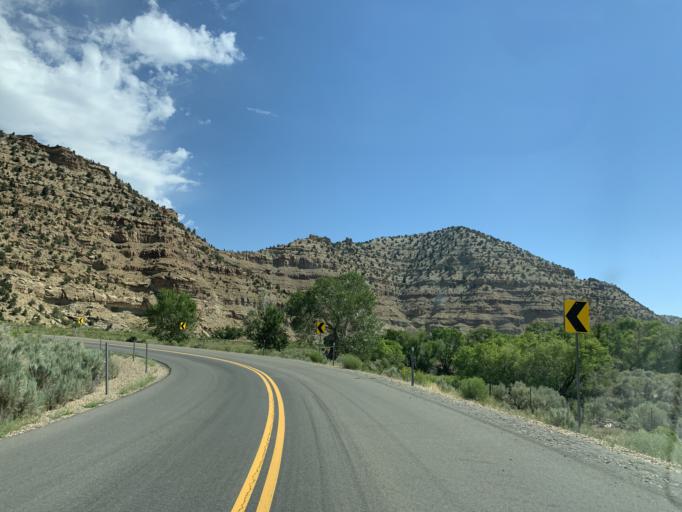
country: US
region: Utah
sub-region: Carbon County
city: East Carbon City
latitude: 39.8008
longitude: -110.3827
